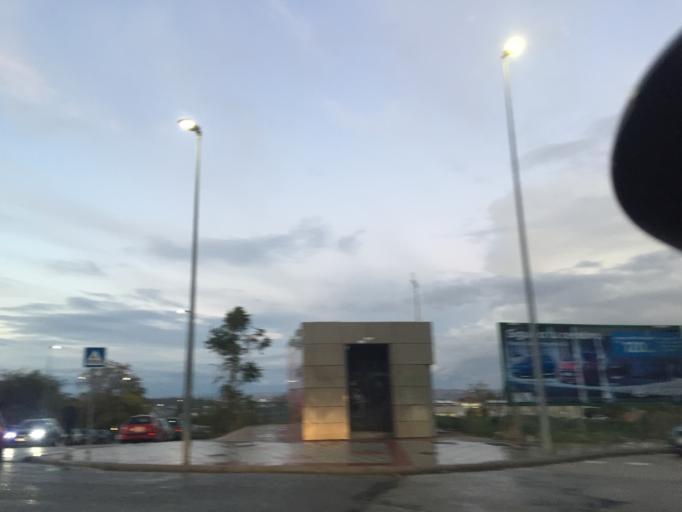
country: ES
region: Andalusia
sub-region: Provincia de Jaen
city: Jaen
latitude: 37.7843
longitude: -3.7854
